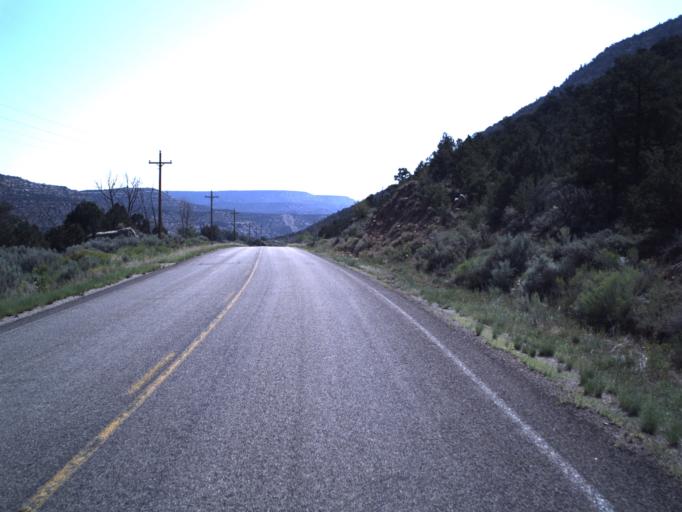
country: US
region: Utah
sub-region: Duchesne County
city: Duchesne
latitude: 40.2960
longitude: -110.5517
